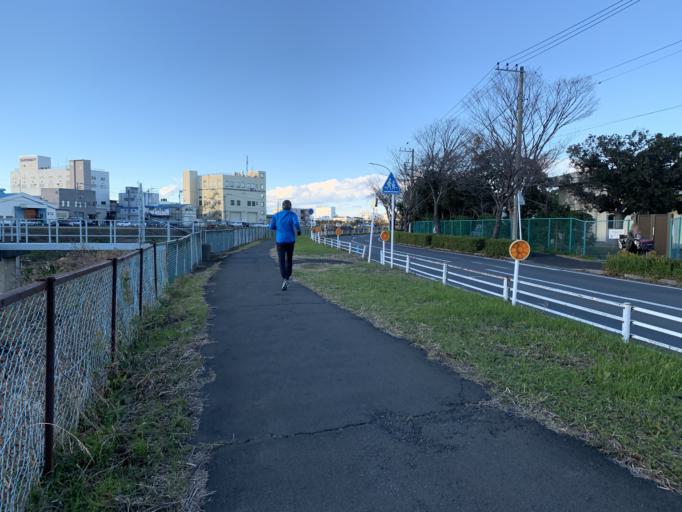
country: JP
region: Tokyo
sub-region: Machida-shi
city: Machida
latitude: 35.5144
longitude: 139.5517
